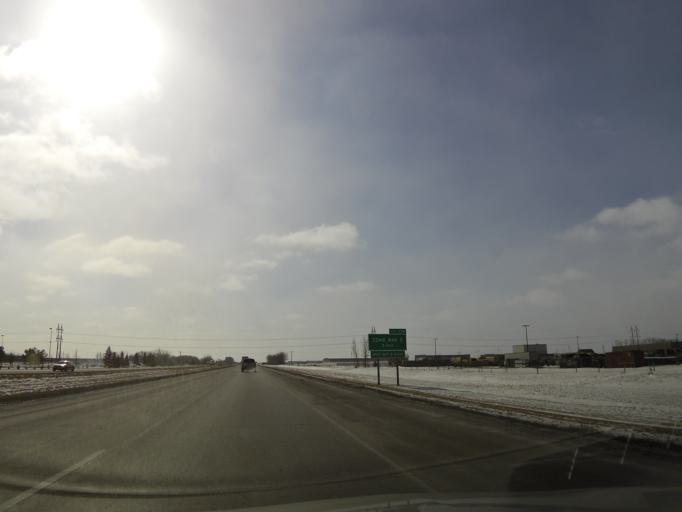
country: US
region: North Dakota
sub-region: Grand Forks County
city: Grand Forks
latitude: 47.9094
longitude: -97.0937
